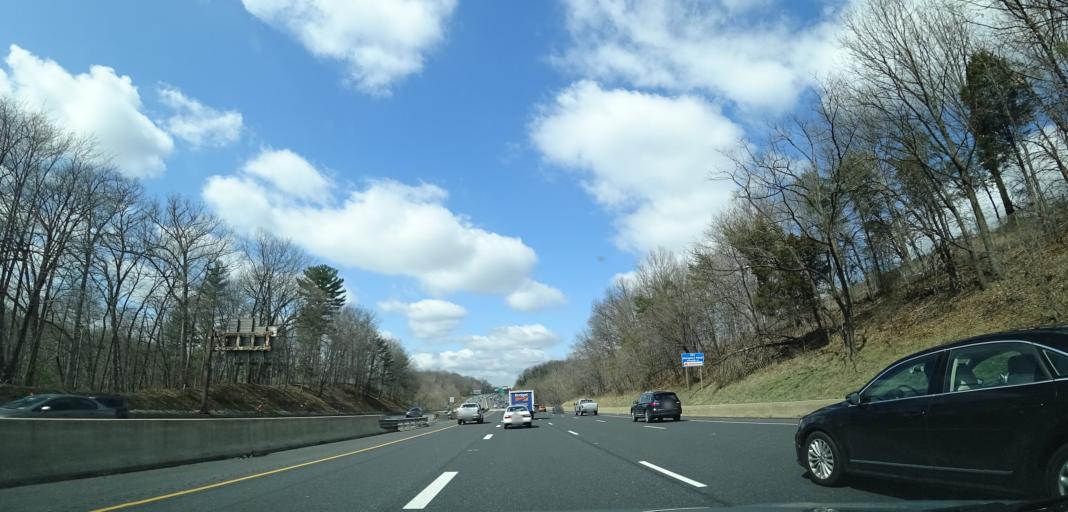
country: US
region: Maryland
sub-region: Montgomery County
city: Gaithersburg
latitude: 39.1599
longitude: -77.2304
